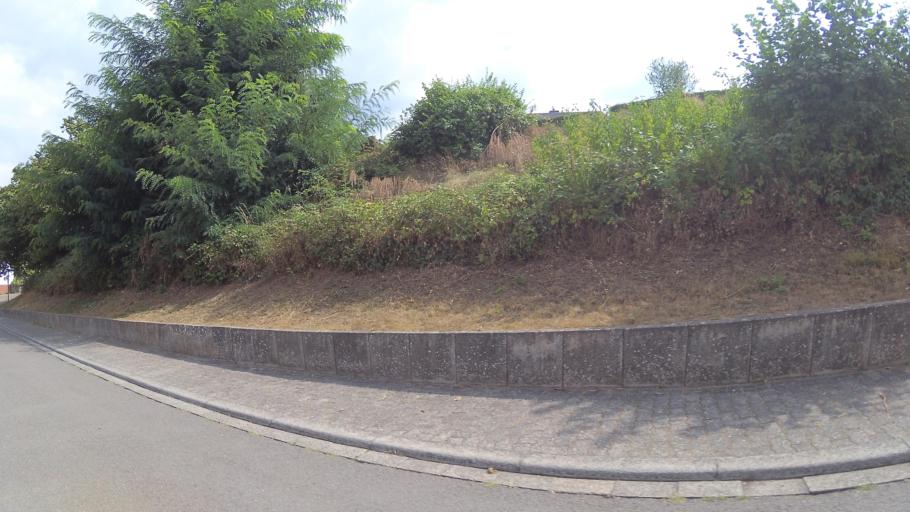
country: DE
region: Rheinland-Pfalz
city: Althornbach
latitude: 49.2023
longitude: 7.3769
